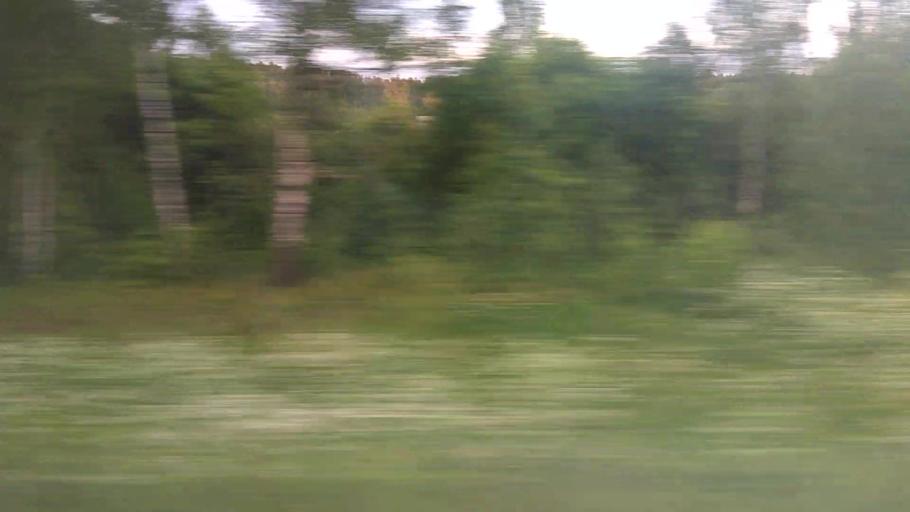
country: RU
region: Moskovskaya
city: Mikhnevo
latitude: 55.1801
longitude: 37.9321
